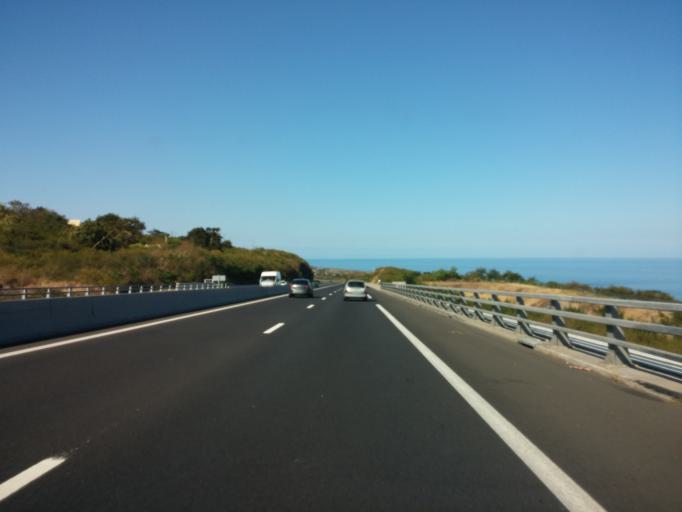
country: RE
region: Reunion
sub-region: Reunion
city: Saint-Leu
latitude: -21.1759
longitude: 55.2972
